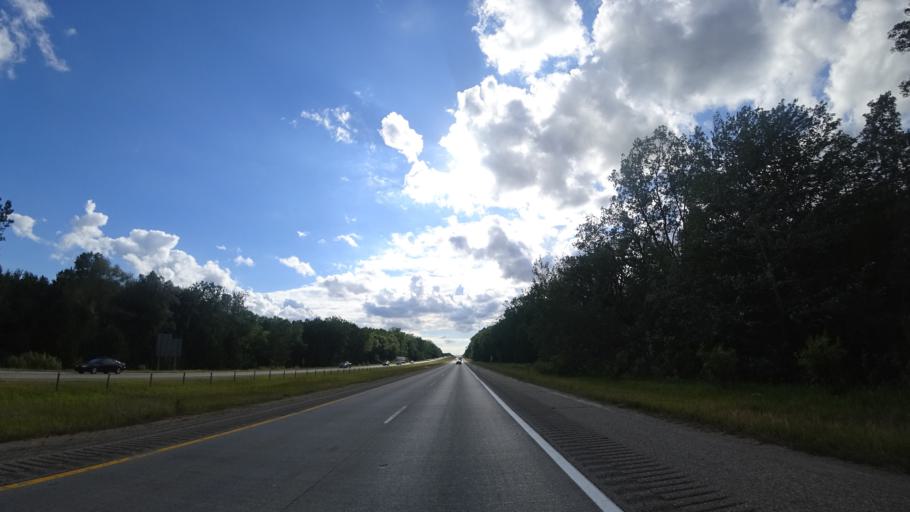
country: US
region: Michigan
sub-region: Kent County
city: Lowell
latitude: 42.8790
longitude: -85.3944
